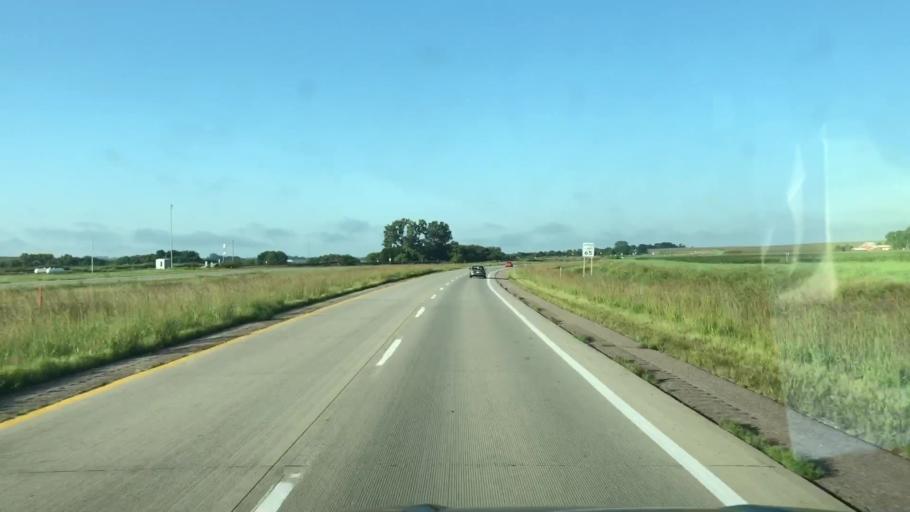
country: US
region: Iowa
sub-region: Sioux County
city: Alton
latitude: 42.9273
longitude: -96.0596
